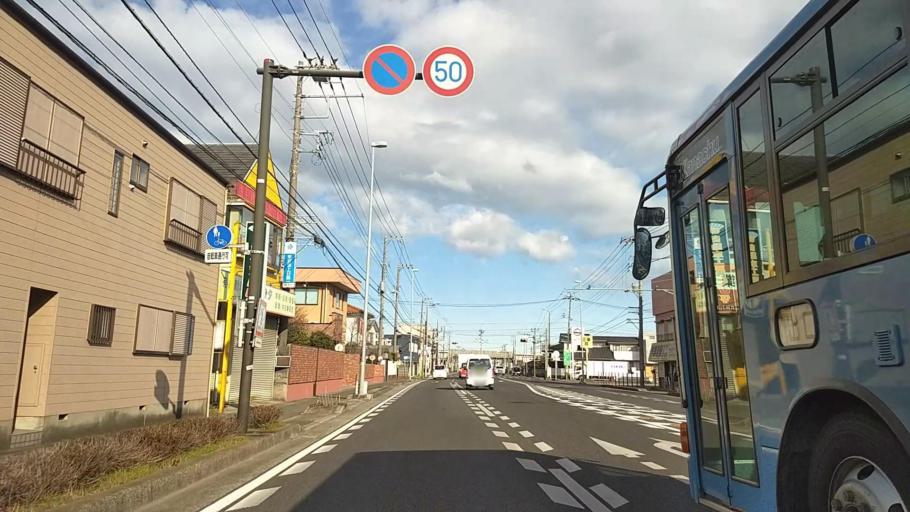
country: JP
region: Kanagawa
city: Isehara
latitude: 35.3828
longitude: 139.3616
